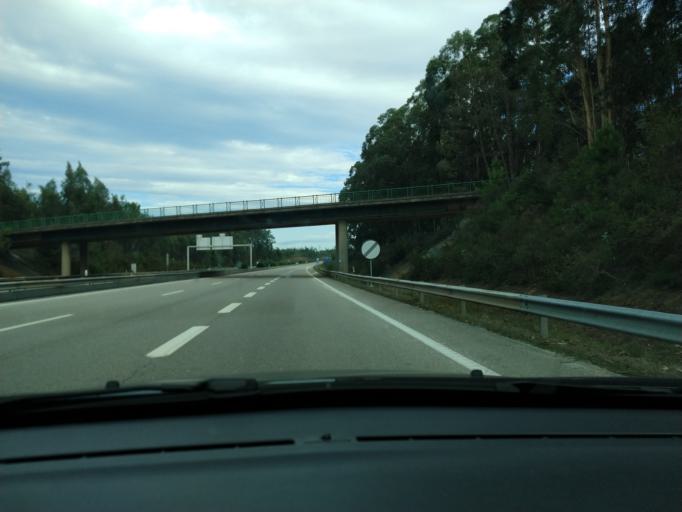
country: PT
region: Aveiro
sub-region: Albergaria-A-Velha
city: Albergaria-a-Velha
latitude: 40.6953
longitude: -8.5228
